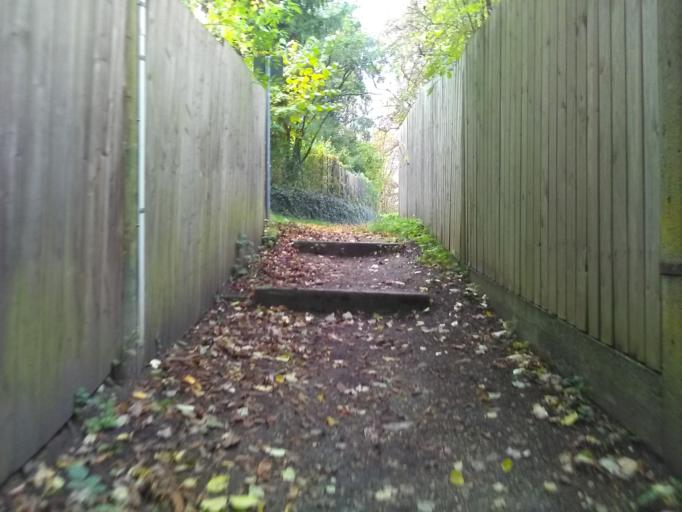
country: DE
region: Bavaria
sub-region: Upper Franconia
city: Bamberg
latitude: 49.8848
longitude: 10.8901
